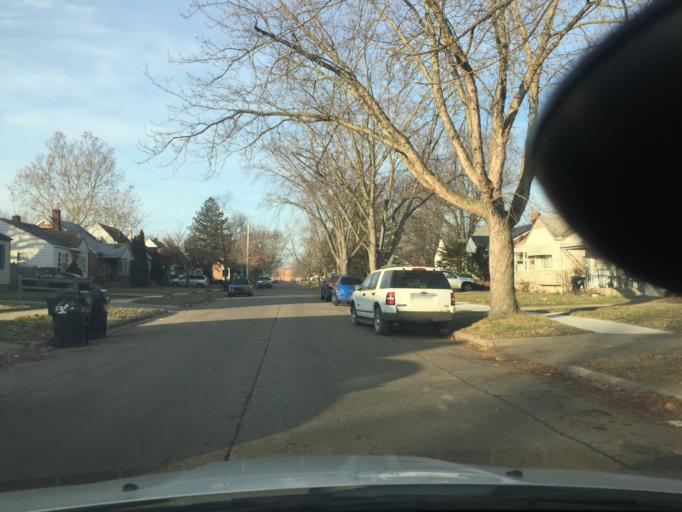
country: US
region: Michigan
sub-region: Macomb County
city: Eastpointe
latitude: 42.4411
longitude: -82.9537
